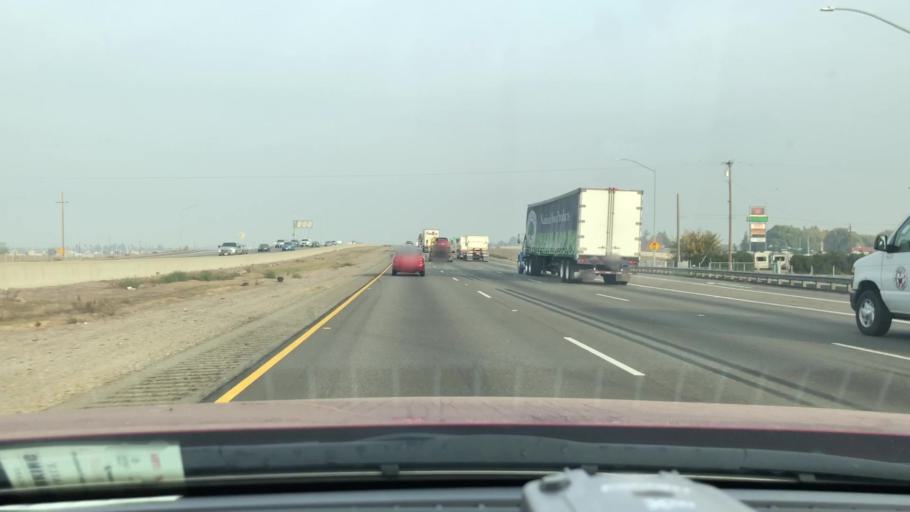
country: US
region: California
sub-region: San Joaquin County
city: French Camp
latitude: 37.8933
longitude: -121.2823
